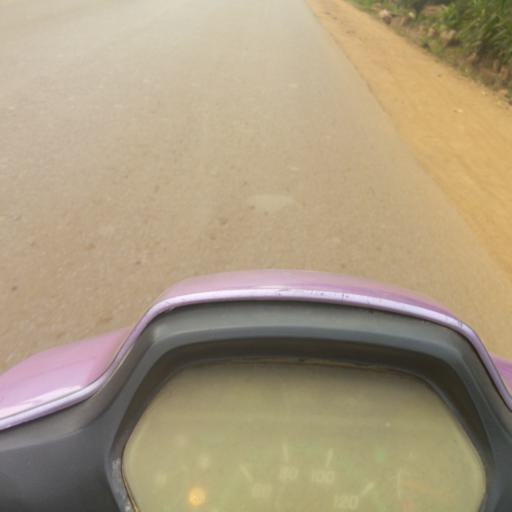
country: ML
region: Bamako
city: Bamako
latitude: 12.6575
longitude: -7.9362
